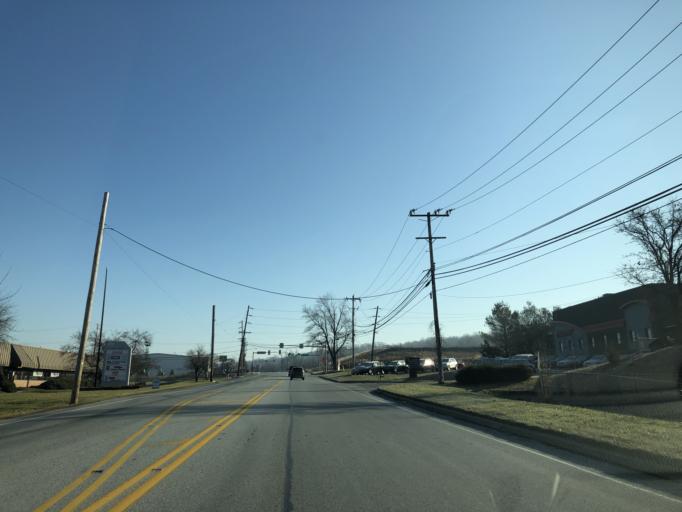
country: US
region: Pennsylvania
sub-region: Chester County
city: Downingtown
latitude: 40.0015
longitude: -75.6963
